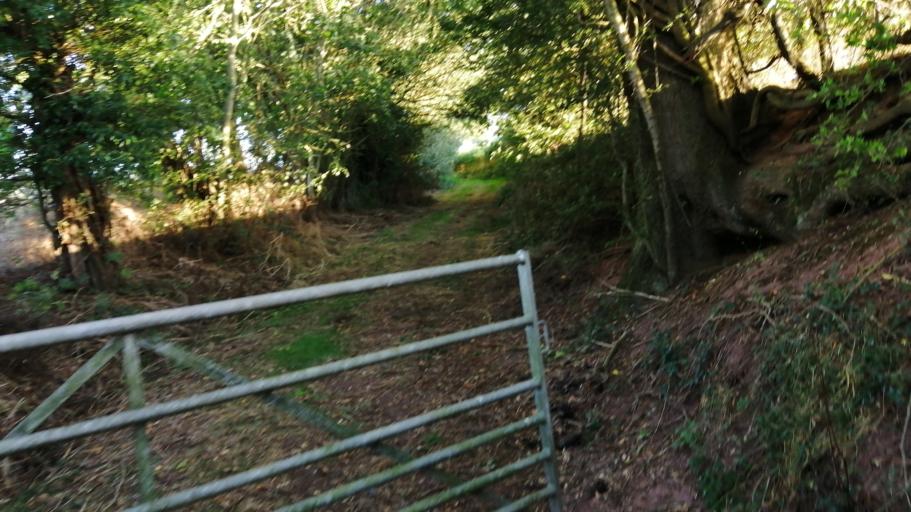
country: GB
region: England
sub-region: Herefordshire
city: Thruxton
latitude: 51.9759
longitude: -2.8008
